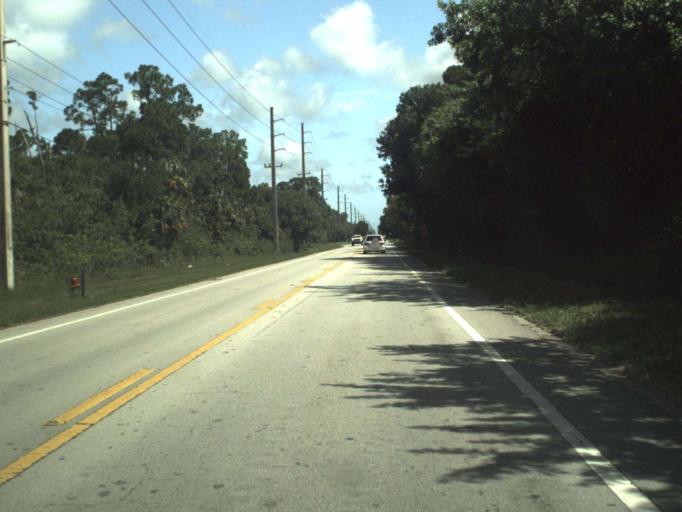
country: US
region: Florida
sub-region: Indian River County
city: Gifford
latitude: 27.6588
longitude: -80.4464
